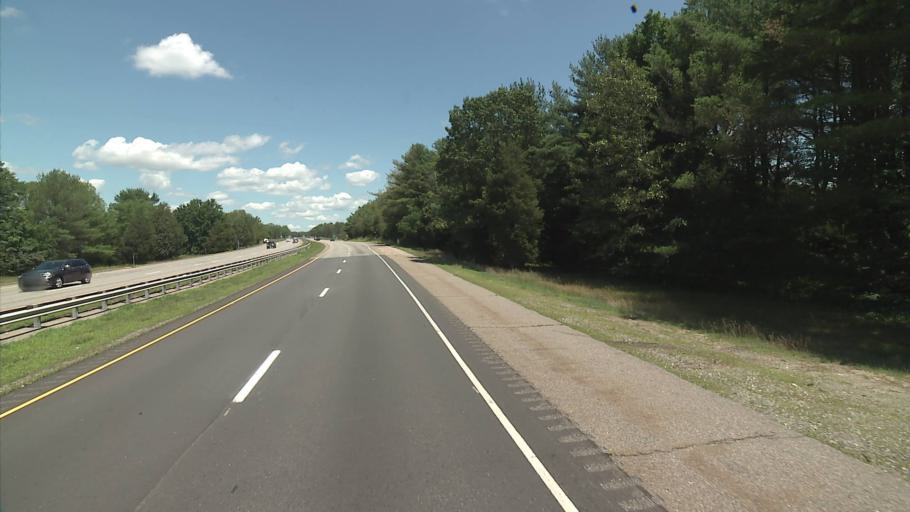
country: US
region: Connecticut
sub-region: New London County
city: Jewett City
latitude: 41.6099
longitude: -71.9469
